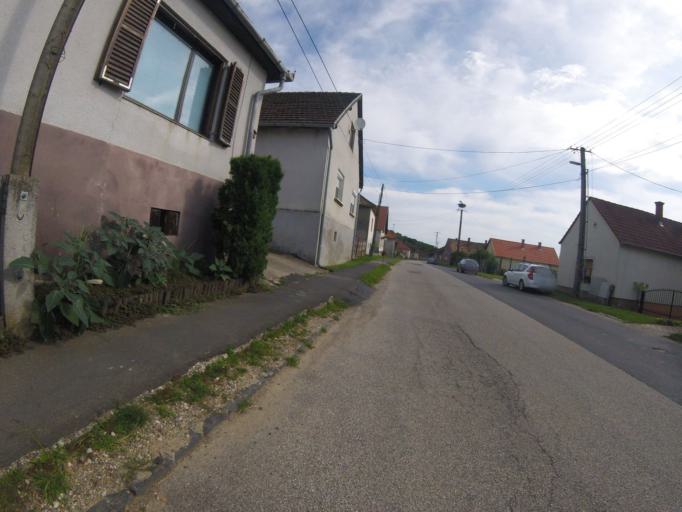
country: HR
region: Medimurska
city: Podturen
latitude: 46.5390
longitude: 16.5920
